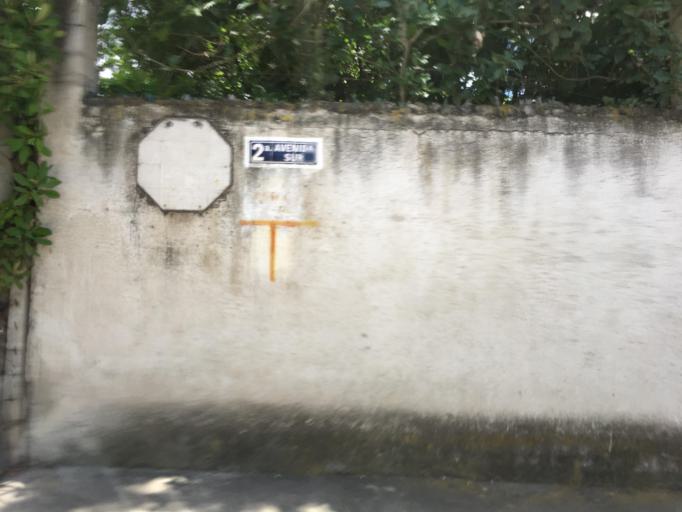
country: GT
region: Sacatepequez
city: Antigua Guatemala
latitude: 14.5491
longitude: -90.7311
